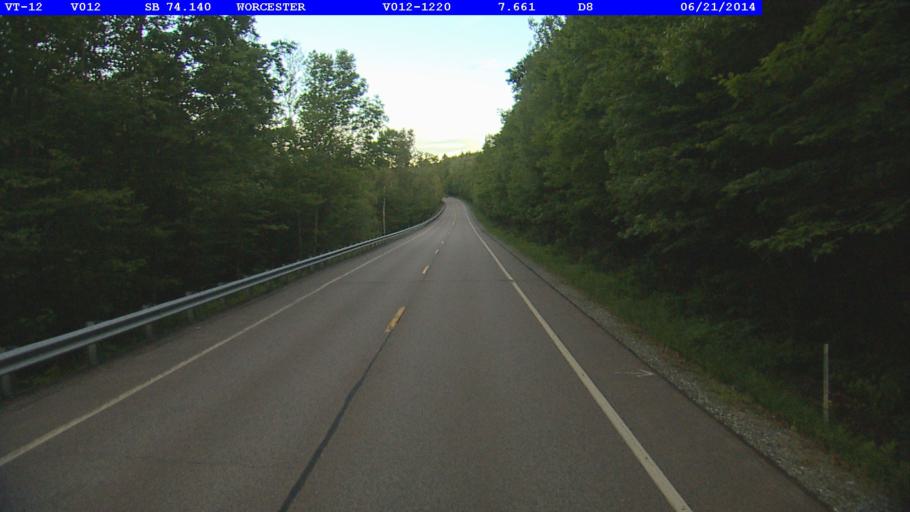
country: US
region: Vermont
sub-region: Lamoille County
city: Morrisville
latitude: 44.4493
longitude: -72.5458
